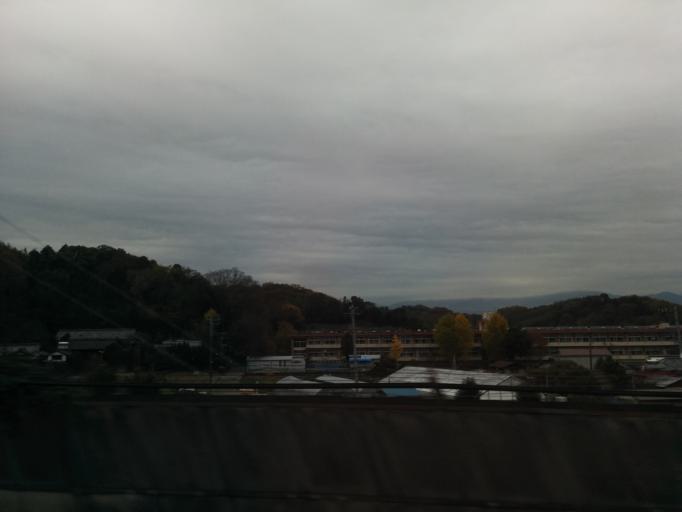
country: JP
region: Kanagawa
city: Ninomiya
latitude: 35.3005
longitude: 139.2259
